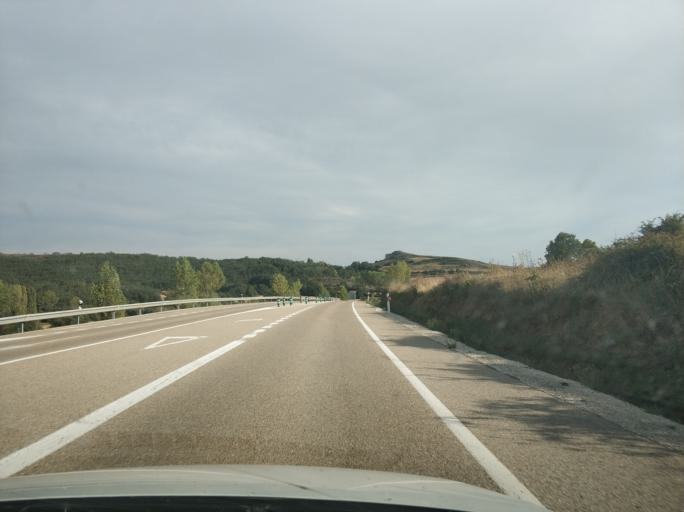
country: ES
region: Castille and Leon
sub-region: Provincia de Burgos
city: Montorio
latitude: 42.5942
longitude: -3.7870
